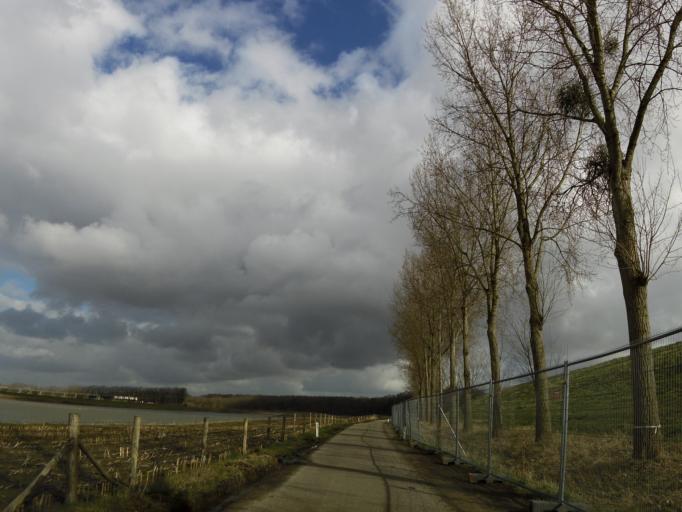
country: NL
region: Limburg
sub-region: Gemeente Stein
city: Elsloo
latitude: 50.9460
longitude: 5.7529
